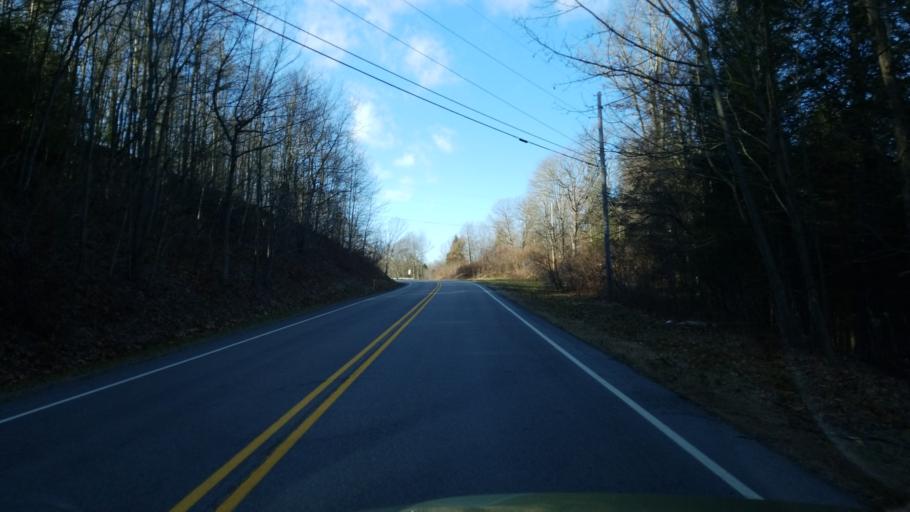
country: US
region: Pennsylvania
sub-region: Clearfield County
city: Hyde
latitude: 41.0007
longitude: -78.4362
